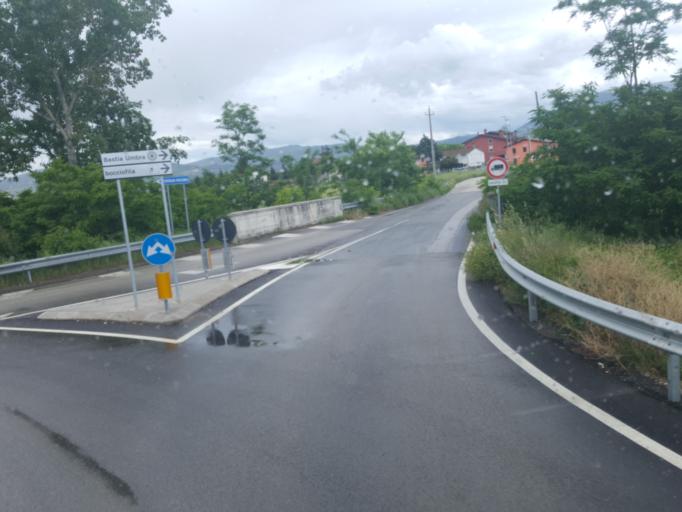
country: IT
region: Umbria
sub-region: Provincia di Perugia
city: Ospedalicchio
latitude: 43.0701
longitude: 12.5119
